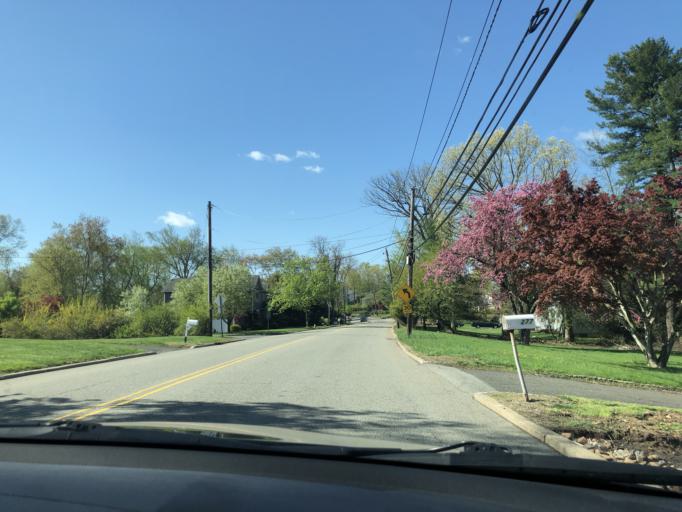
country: US
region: New Jersey
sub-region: Essex County
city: North Caldwell
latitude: 40.8545
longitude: -74.2587
